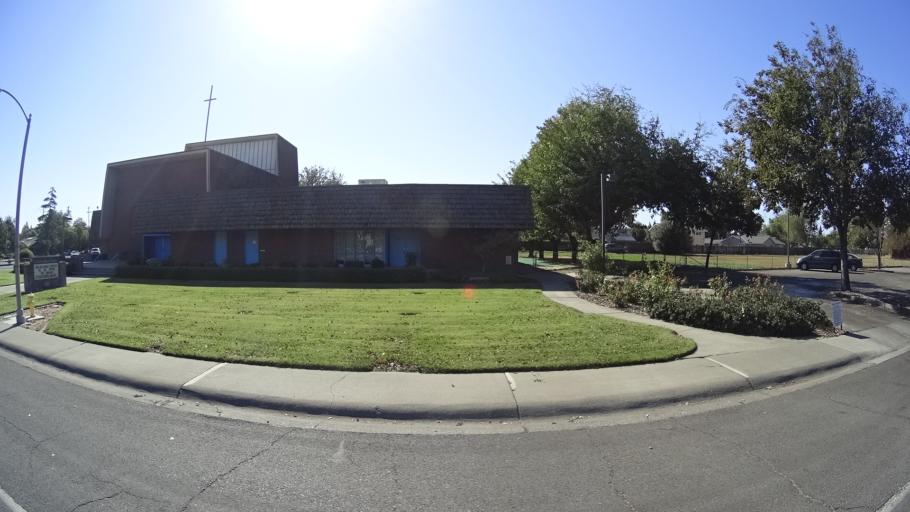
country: US
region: California
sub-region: Yolo County
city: Woodland
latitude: 38.6631
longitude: -121.7946
